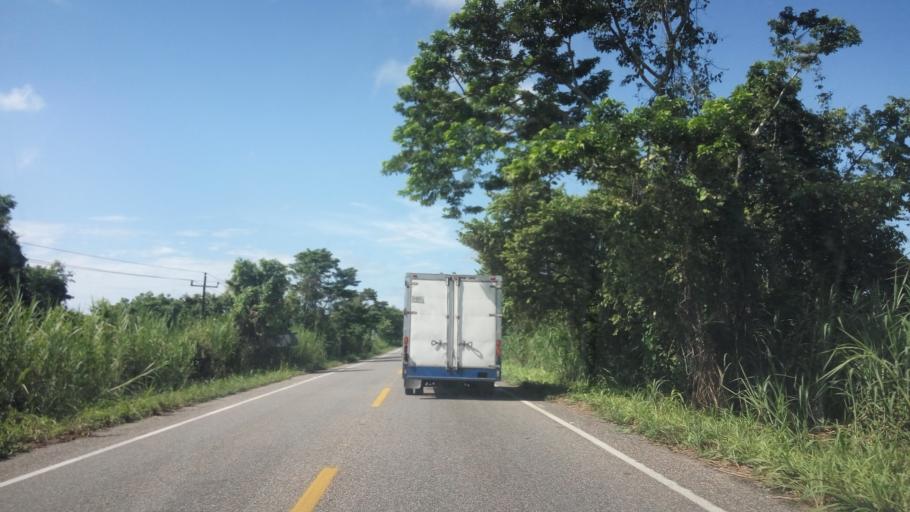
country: MX
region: Tabasco
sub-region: Teapa
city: Eureka y Belen
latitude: 17.6748
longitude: -92.9463
